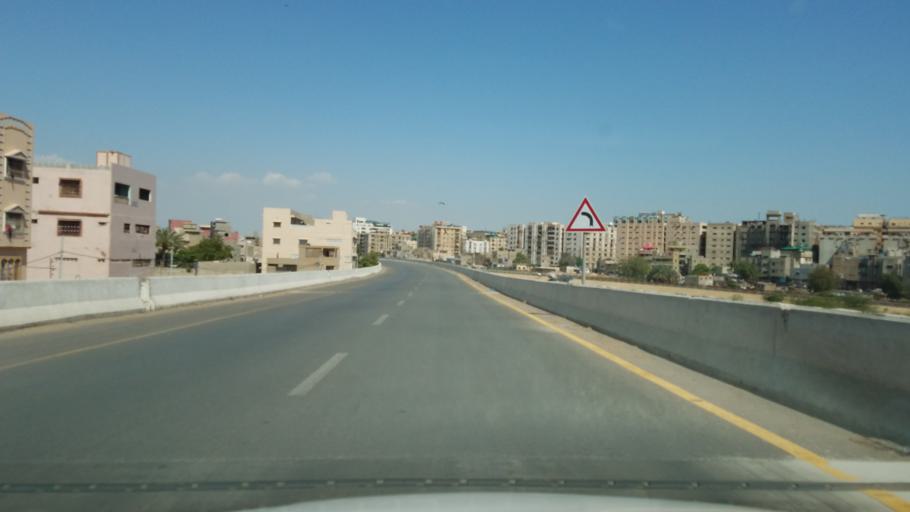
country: PK
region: Sindh
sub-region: Karachi District
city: Karachi
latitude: 24.8795
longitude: 67.0137
